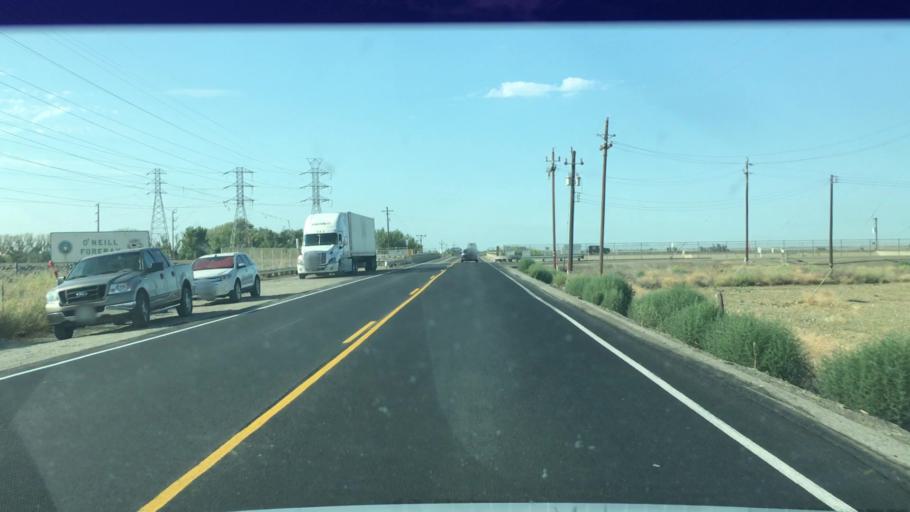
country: US
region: California
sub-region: Merced County
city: Los Banos
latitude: 37.0731
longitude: -121.0162
